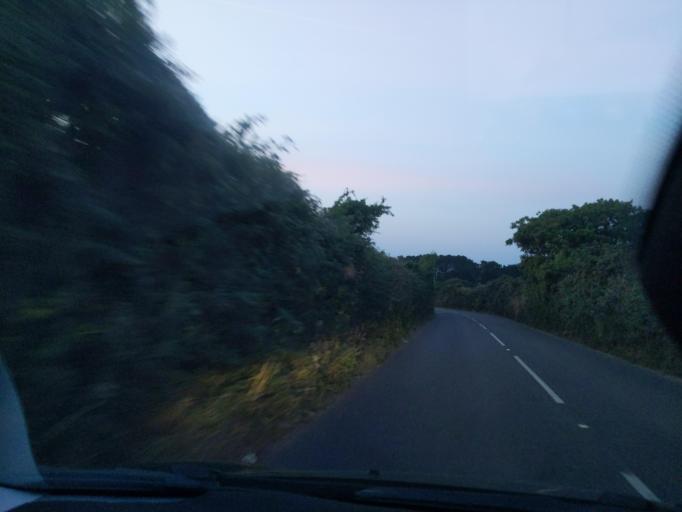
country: GB
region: England
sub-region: Cornwall
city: Camborne
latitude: 50.1889
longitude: -5.3075
